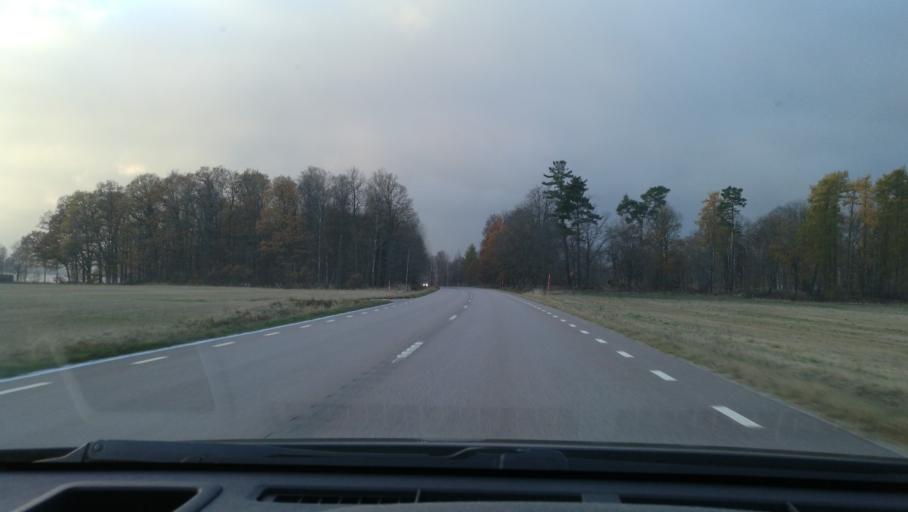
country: SE
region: Soedermanland
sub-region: Vingakers Kommun
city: Vingaker
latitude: 59.1571
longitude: 16.0270
